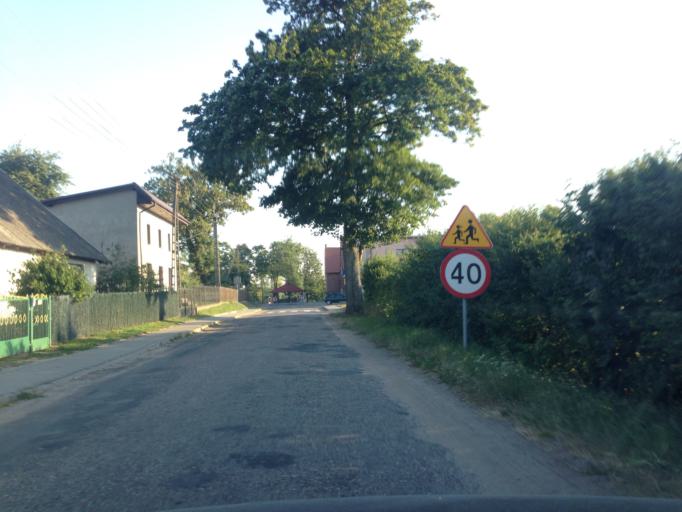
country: PL
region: Kujawsko-Pomorskie
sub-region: Powiat brodnicki
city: Brzozie
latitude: 53.2889
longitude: 19.6910
